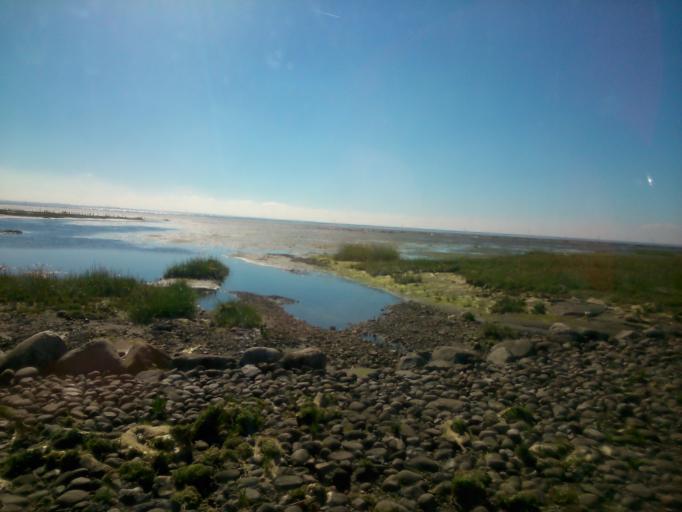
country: DK
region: South Denmark
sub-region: Esbjerg Kommune
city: Ribe
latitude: 55.2982
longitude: 8.6094
